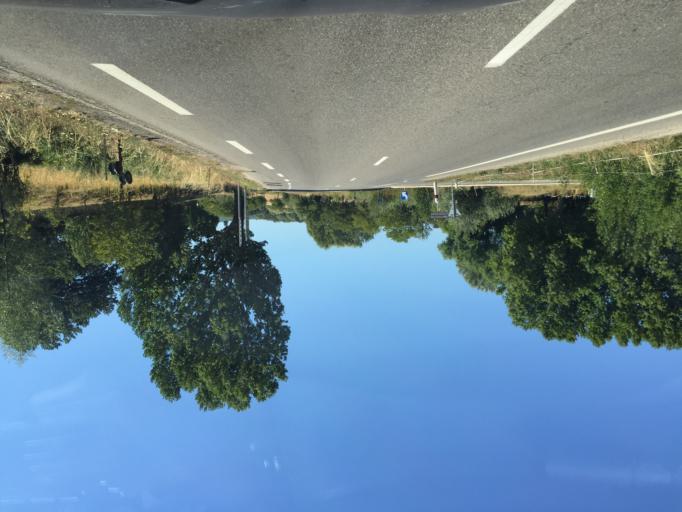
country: FR
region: Provence-Alpes-Cote d'Azur
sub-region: Departement des Alpes-de-Haute-Provence
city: Reillanne
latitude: 43.8634
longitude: 5.6624
